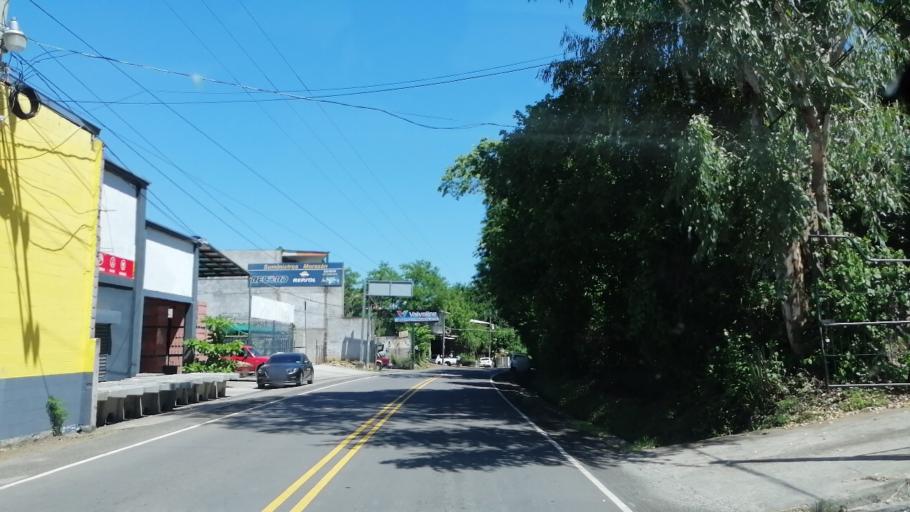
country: SV
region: Morazan
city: Cacaopera
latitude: 13.8065
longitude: -88.1453
